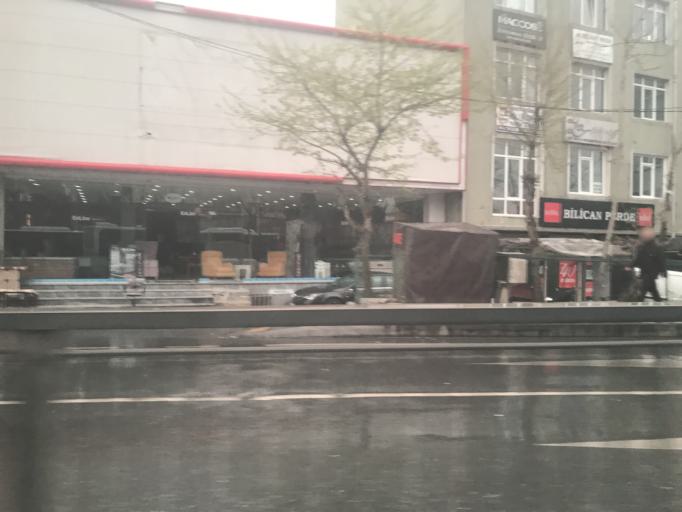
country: TR
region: Istanbul
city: Sisli
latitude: 41.0532
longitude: 28.9617
